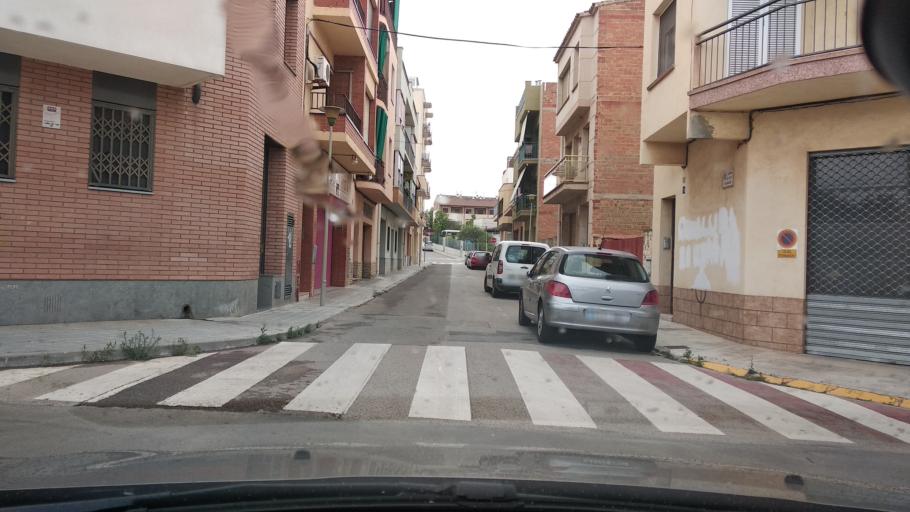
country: ES
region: Catalonia
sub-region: Provincia de Tarragona
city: El Vendrell
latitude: 41.2155
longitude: 1.5271
